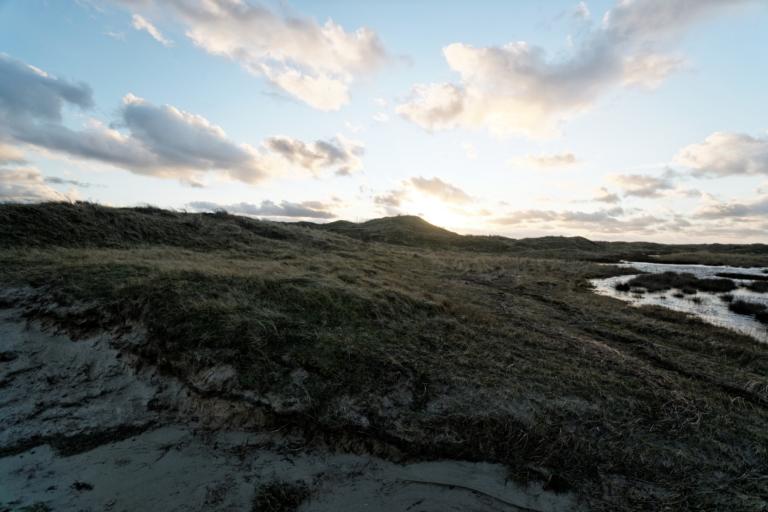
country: NL
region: North Holland
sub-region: Gemeente Texel
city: Den Burg
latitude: 53.1324
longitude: 4.8044
